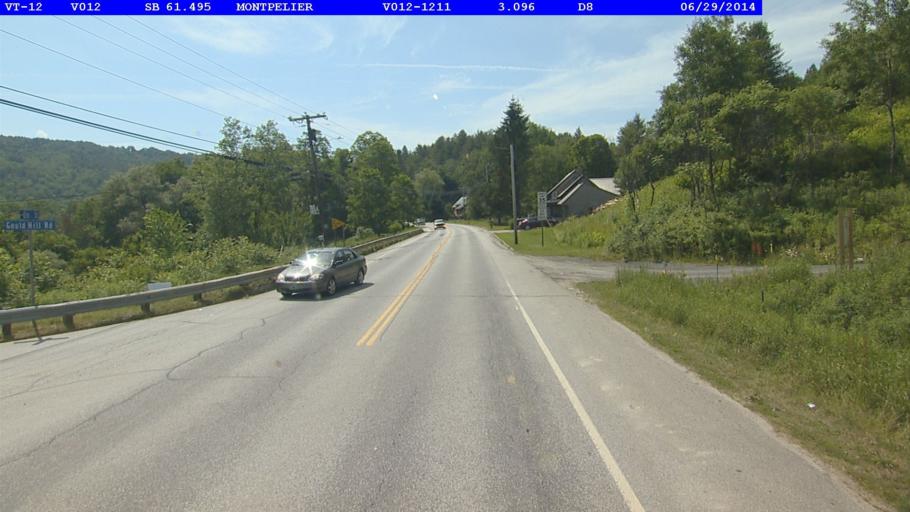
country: US
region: Vermont
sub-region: Washington County
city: Montpelier
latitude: 44.2867
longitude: -72.5780
